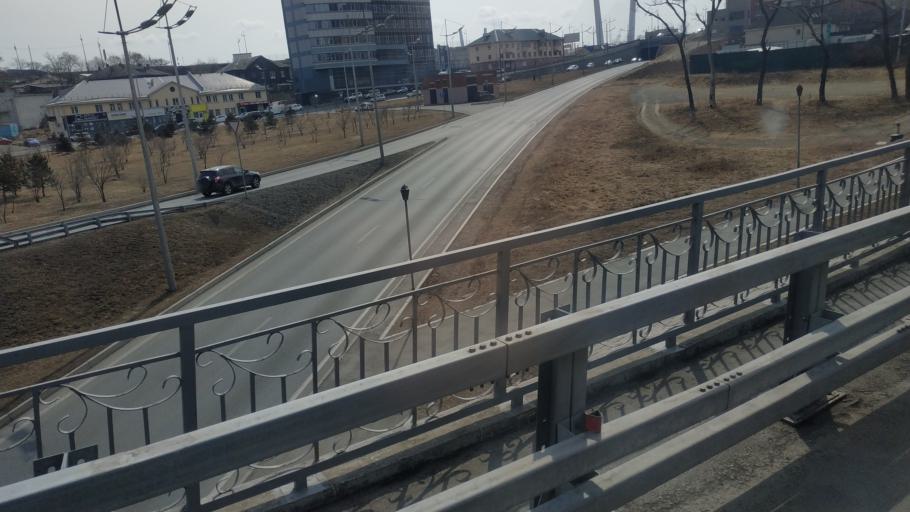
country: RU
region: Primorskiy
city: Vladivostok
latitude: 43.1209
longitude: 131.9032
